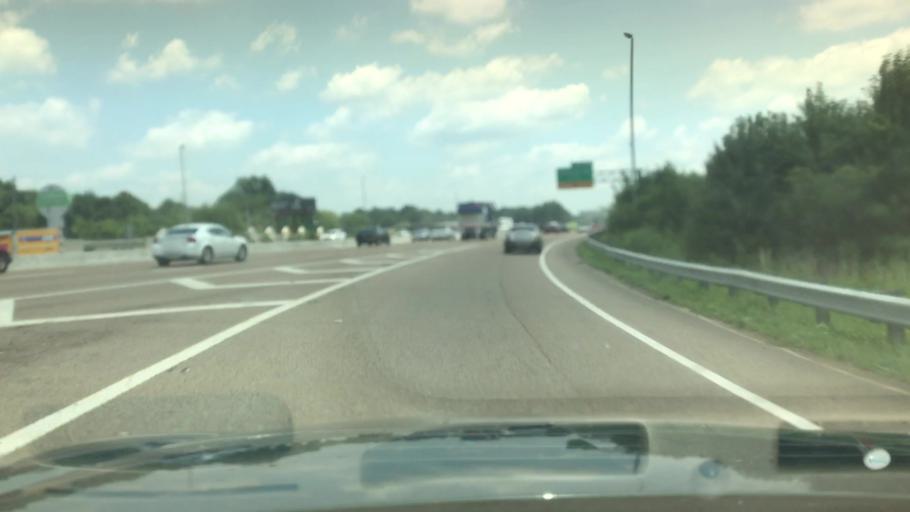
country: US
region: Tennessee
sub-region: Shelby County
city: Germantown
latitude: 35.0794
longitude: -89.9280
